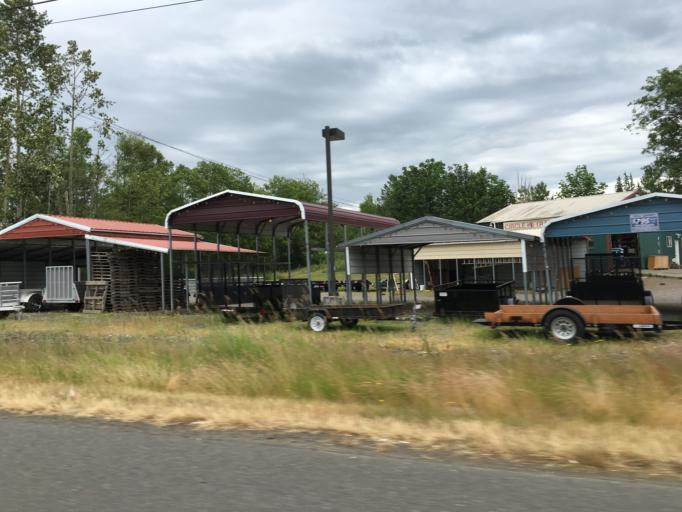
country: US
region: Washington
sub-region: Whatcom County
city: Bellingham
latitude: 48.8270
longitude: -122.4859
